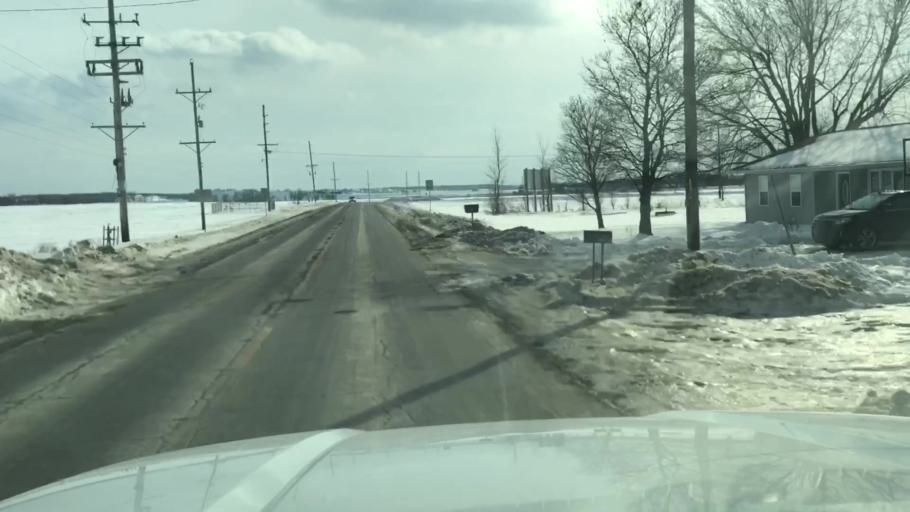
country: US
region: Missouri
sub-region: Gentry County
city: Stanberry
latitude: 40.3480
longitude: -94.6733
